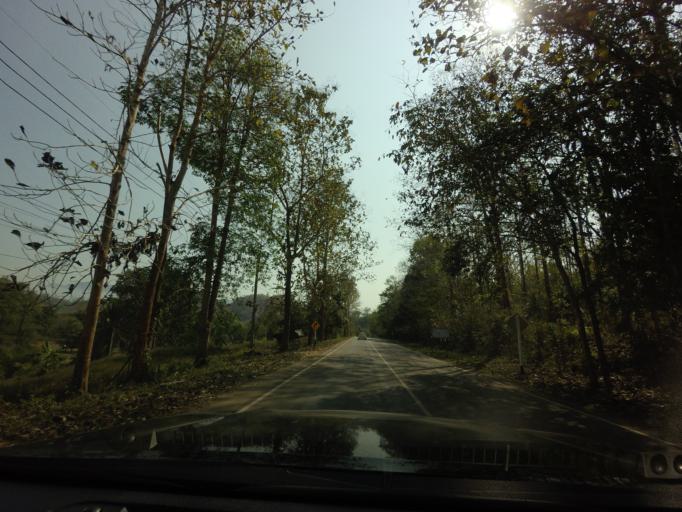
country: TH
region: Kanchanaburi
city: Thong Pha Phum
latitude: 14.6572
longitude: 98.5380
